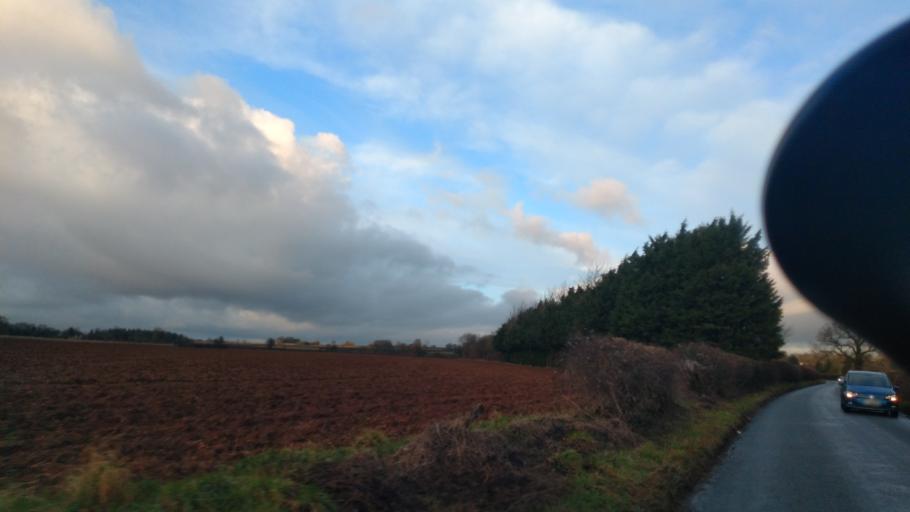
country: GB
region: England
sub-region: Wiltshire
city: Biddestone
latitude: 51.4519
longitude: -2.1882
